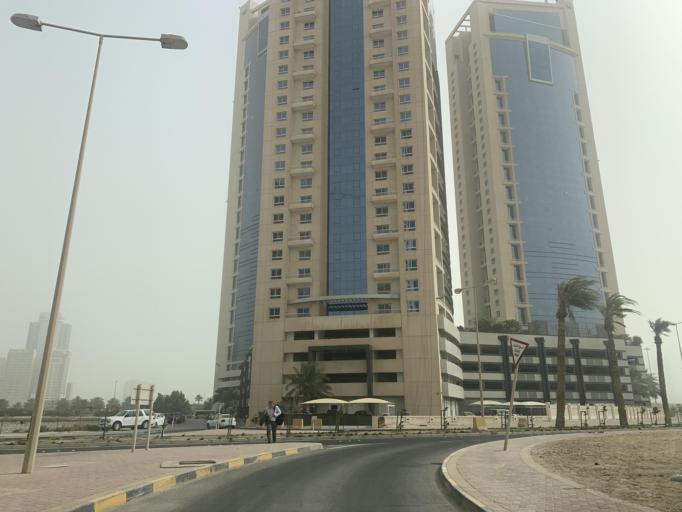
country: BH
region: Manama
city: Jidd Hafs
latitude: 26.2288
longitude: 50.5584
